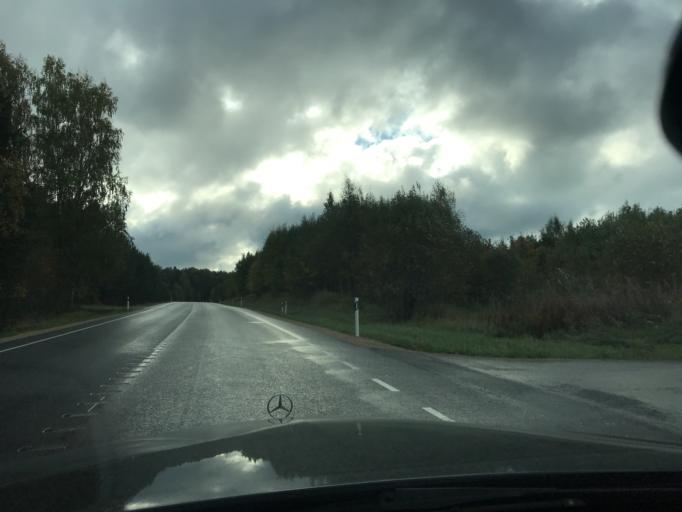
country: EE
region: Viljandimaa
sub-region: Karksi vald
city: Karksi-Nuia
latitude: 58.0554
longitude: 25.6330
